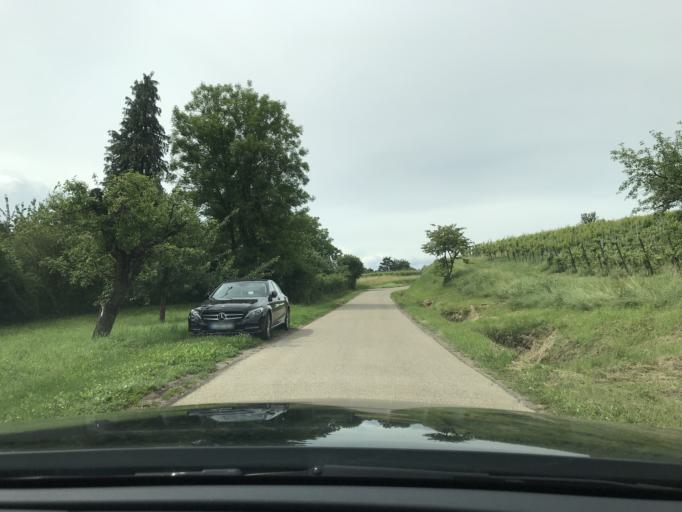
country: DE
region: Baden-Wuerttemberg
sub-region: Regierungsbezirk Stuttgart
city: Weinstadt-Endersbach
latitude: 48.7973
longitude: 9.3618
